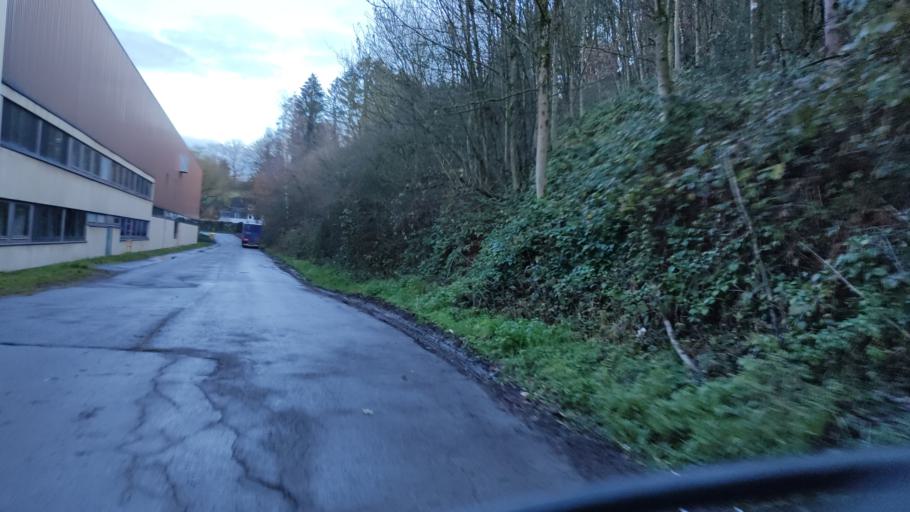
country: DE
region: North Rhine-Westphalia
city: Hattingen
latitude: 51.3741
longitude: 7.1275
